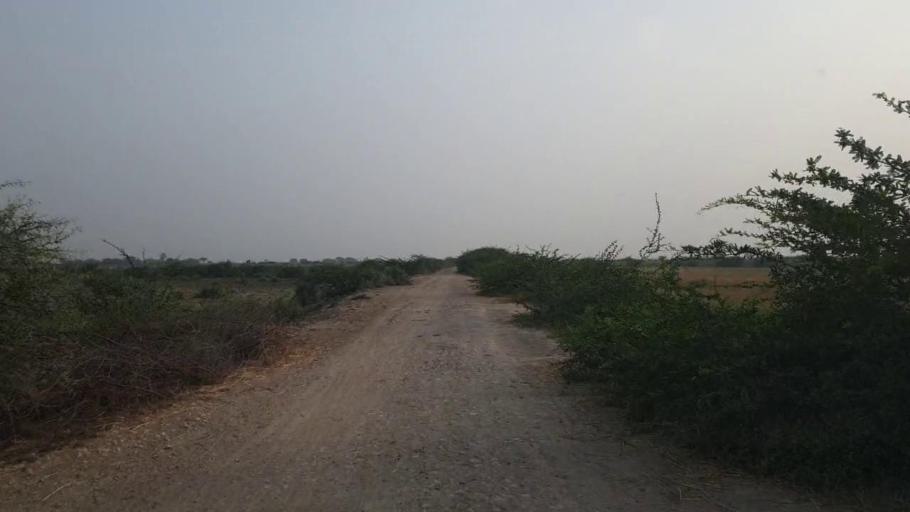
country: PK
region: Sindh
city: Mirpur Batoro
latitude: 24.6464
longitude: 68.3727
